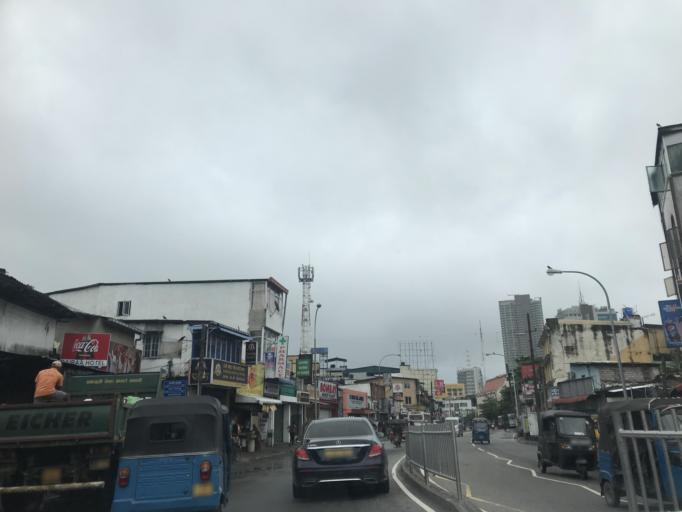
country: LK
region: Western
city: Colombo
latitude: 6.9252
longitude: 79.8653
